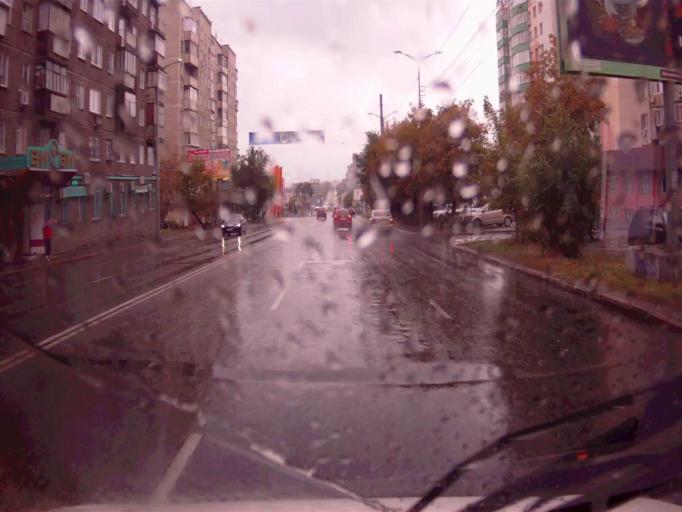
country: RU
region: Chelyabinsk
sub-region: Gorod Chelyabinsk
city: Chelyabinsk
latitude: 55.1617
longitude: 61.4163
